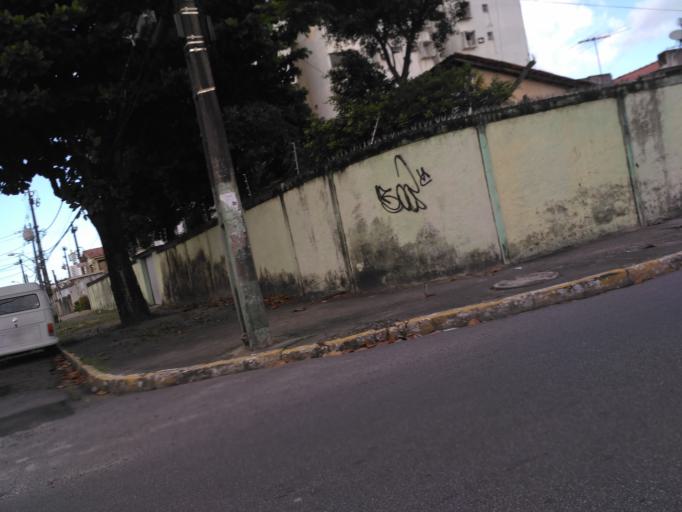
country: BR
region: Pernambuco
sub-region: Recife
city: Recife
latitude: -8.0507
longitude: -34.9411
